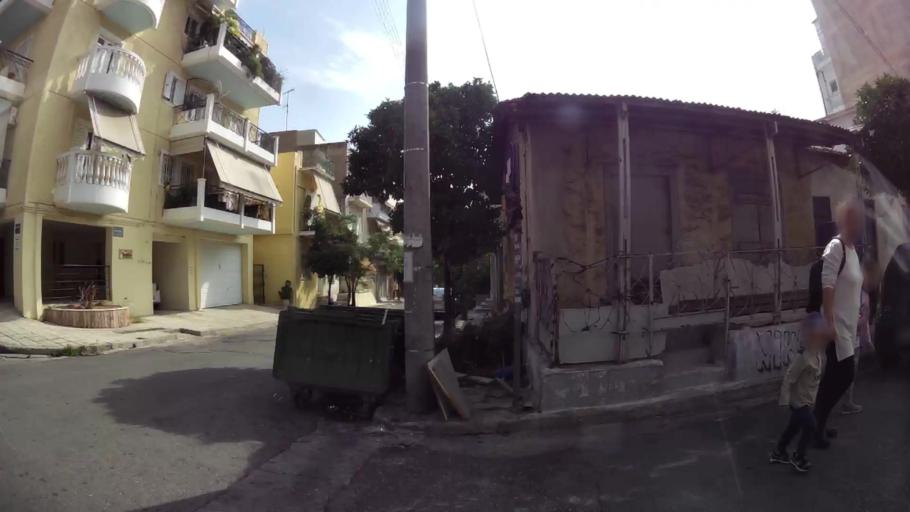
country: GR
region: Attica
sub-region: Nomos Piraios
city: Nikaia
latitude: 37.9648
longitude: 23.6420
